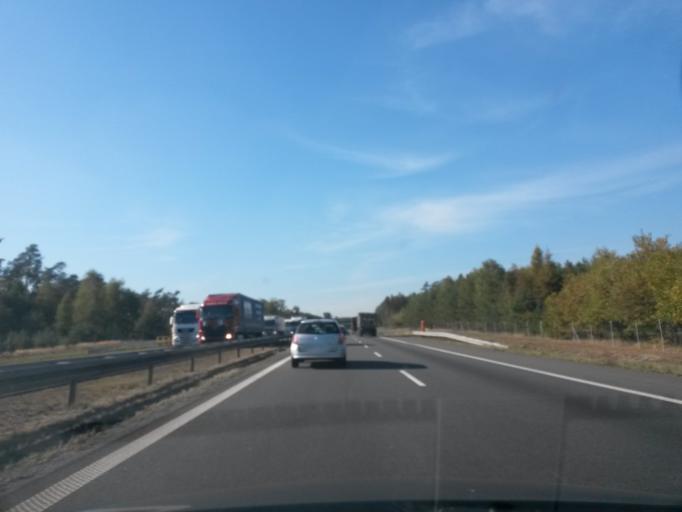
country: PL
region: Opole Voivodeship
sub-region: Powiat opolski
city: Komprachcice
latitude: 50.5896
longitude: 17.8117
